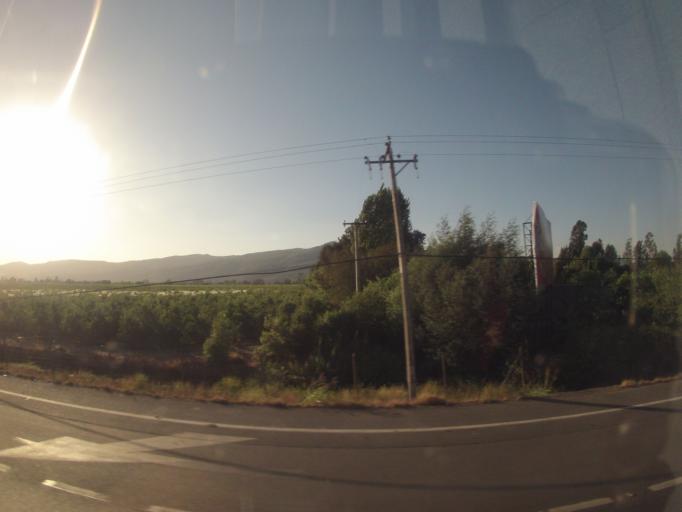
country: CL
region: O'Higgins
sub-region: Provincia de Colchagua
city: Chimbarongo
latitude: -34.6979
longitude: -71.0205
